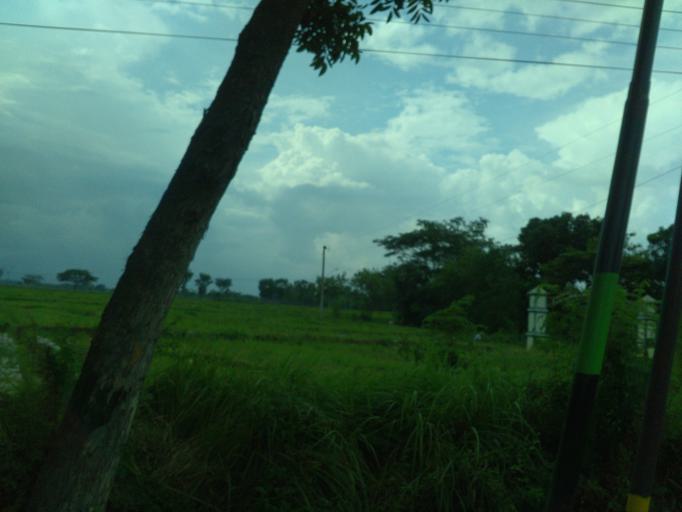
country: ID
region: Central Java
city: Ceper
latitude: -7.6527
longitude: 110.6822
